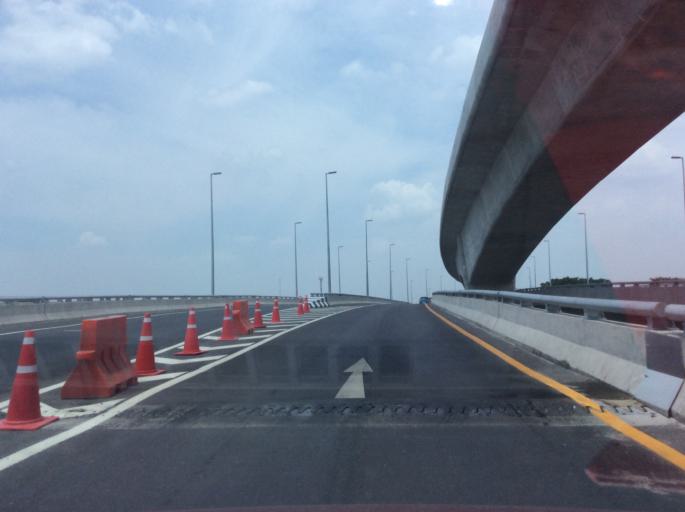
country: TH
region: Bangkok
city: Sai Mai
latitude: 13.9321
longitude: 100.6381
